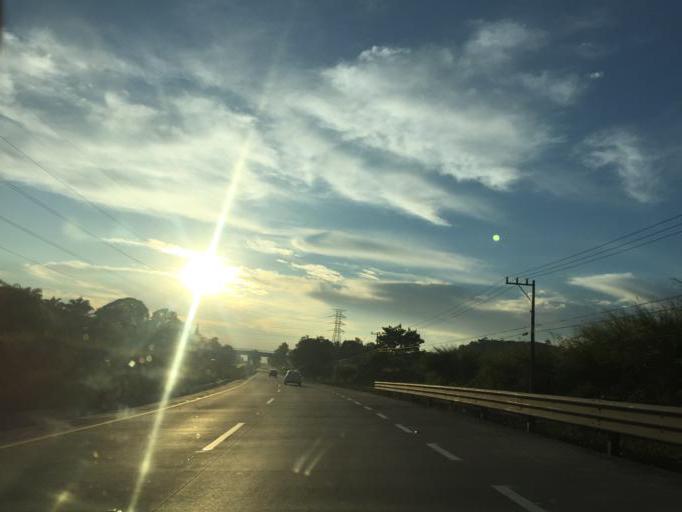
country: MX
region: Veracruz
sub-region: Fortin
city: Cordoba (Santa Leticia)
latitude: 18.8978
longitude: -96.9827
